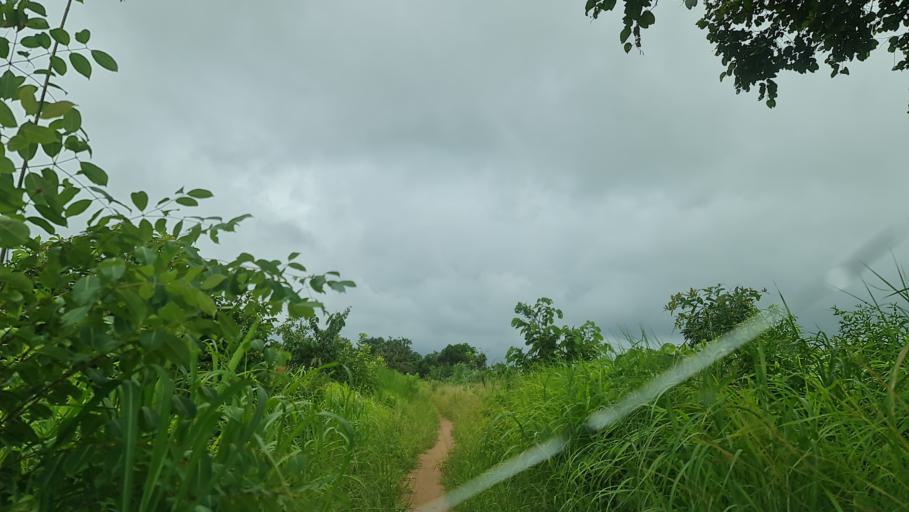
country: MW
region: Southern Region
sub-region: Nsanje District
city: Nsanje
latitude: -17.3951
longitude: 35.7858
